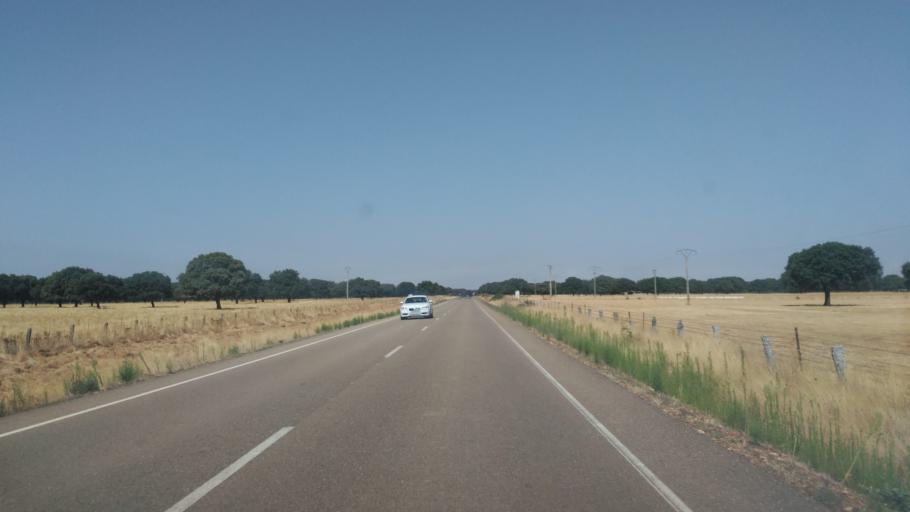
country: ES
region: Castille and Leon
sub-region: Provincia de Salamanca
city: Tamames
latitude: 40.6776
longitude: -6.1263
